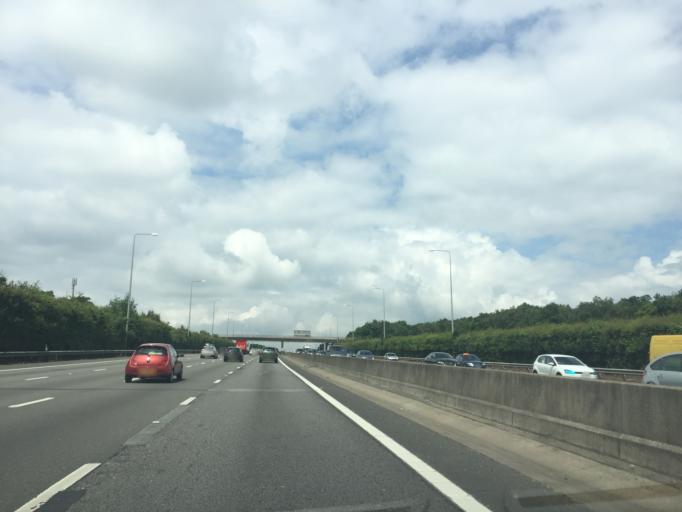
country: GB
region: England
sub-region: Buckinghamshire
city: Gerrards Cross
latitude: 51.5863
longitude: -0.5339
